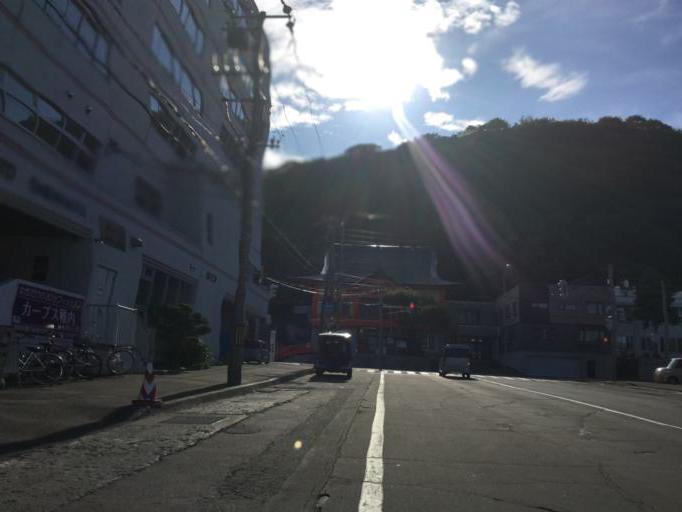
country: JP
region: Hokkaido
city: Wakkanai
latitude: 45.4097
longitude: 141.6747
